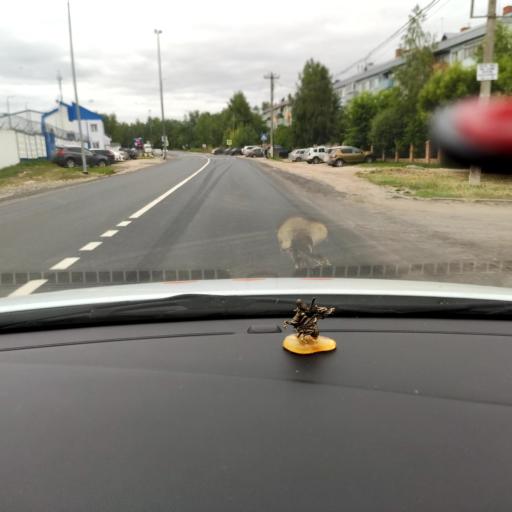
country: RU
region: Tatarstan
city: Stolbishchi
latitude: 55.6210
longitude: 49.1567
